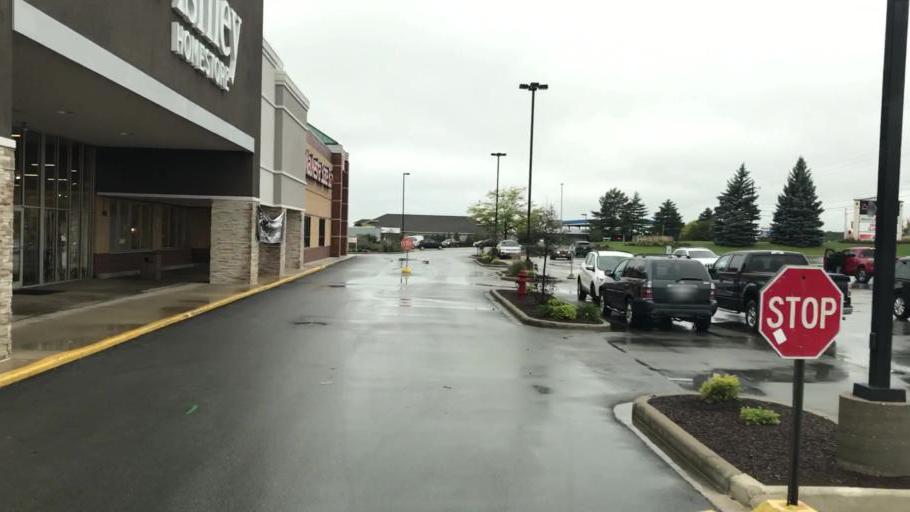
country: US
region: Wisconsin
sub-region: Waukesha County
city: Pewaukee
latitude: 43.0822
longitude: -88.2378
